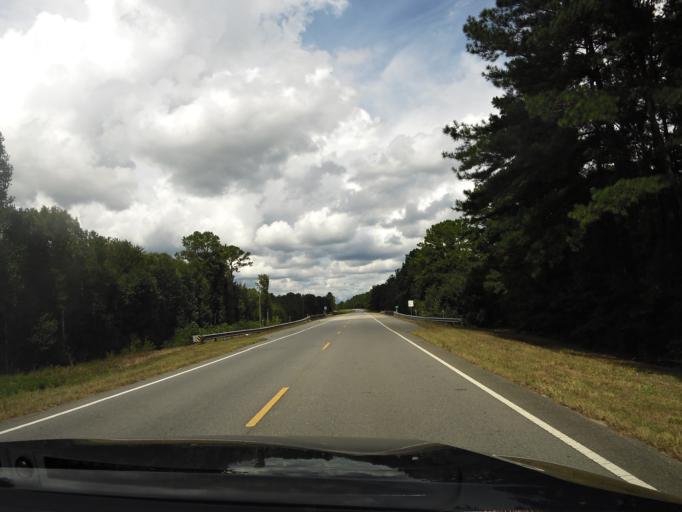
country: US
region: Georgia
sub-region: Brantley County
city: Nahunta
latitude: 31.0968
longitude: -82.0061
